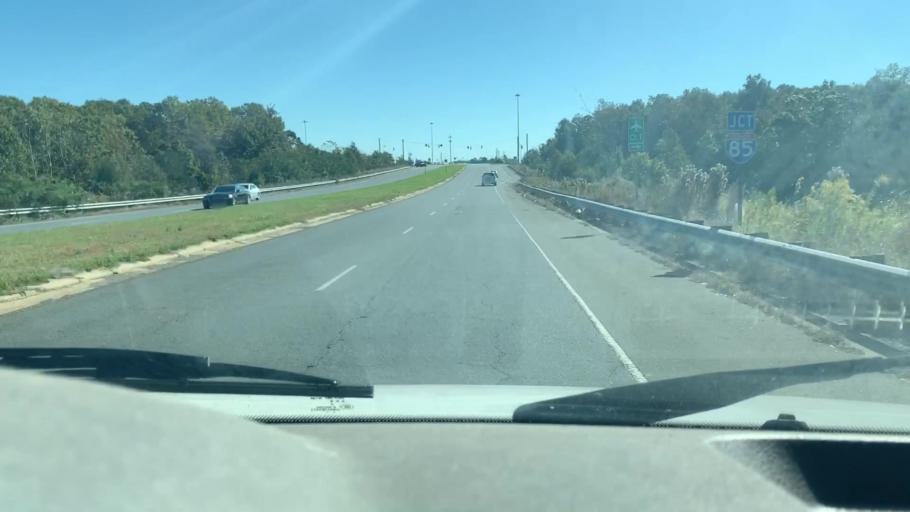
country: US
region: North Carolina
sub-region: Mecklenburg County
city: Charlotte
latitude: 35.2925
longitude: -80.7737
